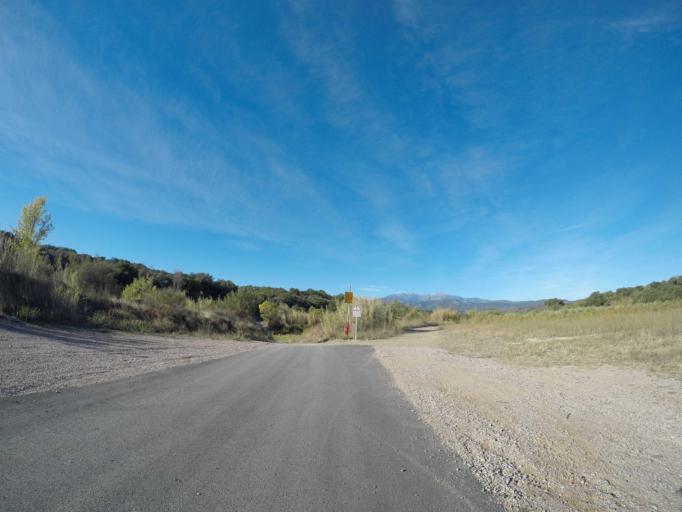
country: FR
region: Languedoc-Roussillon
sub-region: Departement des Pyrenees-Orientales
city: Llupia
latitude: 42.6042
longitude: 2.7695
